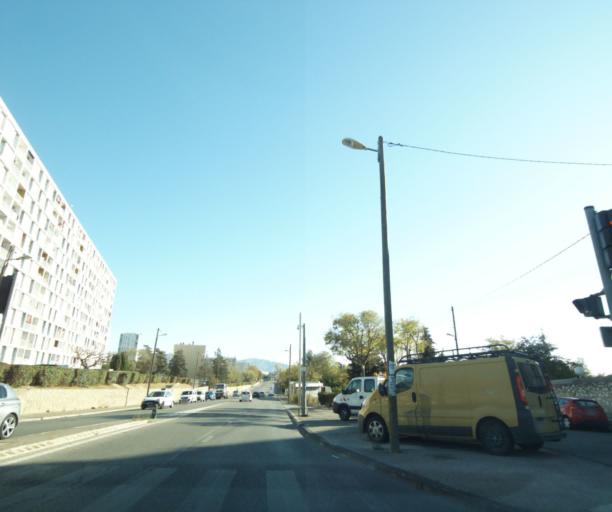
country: FR
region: Provence-Alpes-Cote d'Azur
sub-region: Departement des Bouches-du-Rhone
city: Marseille 14
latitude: 43.3529
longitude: 5.3722
